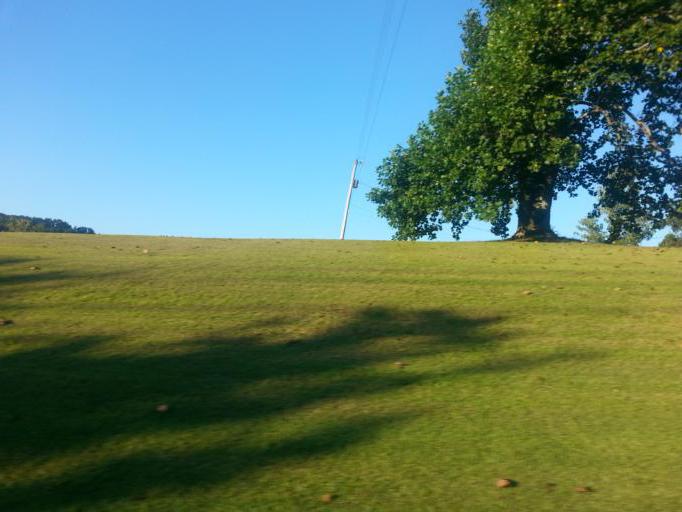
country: US
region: Tennessee
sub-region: Blount County
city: Wildwood
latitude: 35.8572
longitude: -83.8831
